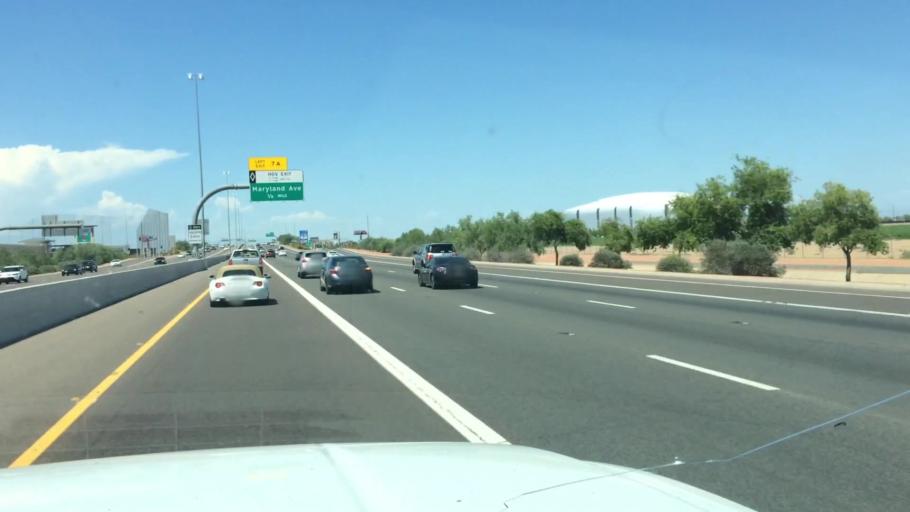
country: US
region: Arizona
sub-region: Maricopa County
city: Tolleson
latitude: 33.5180
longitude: -112.2677
